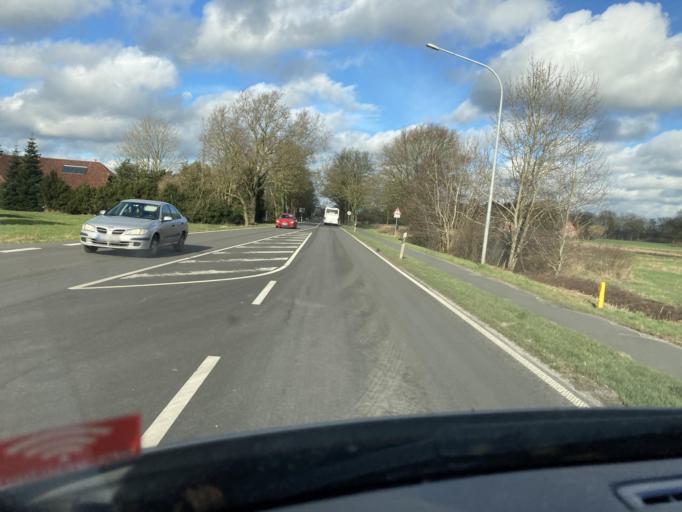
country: DE
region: Lower Saxony
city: Ostrhauderfehn
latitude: 53.1488
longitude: 7.5635
